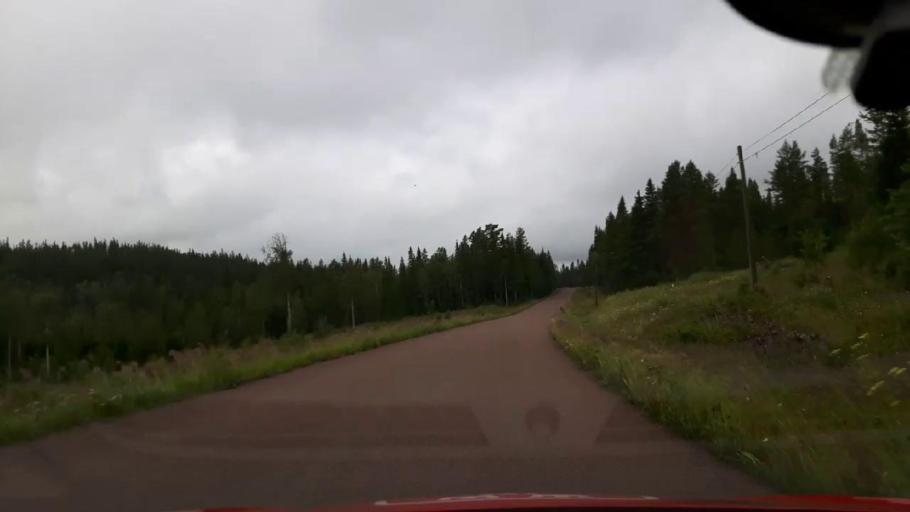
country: SE
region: Jaemtland
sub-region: Krokoms Kommun
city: Valla
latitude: 63.3898
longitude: 13.8510
